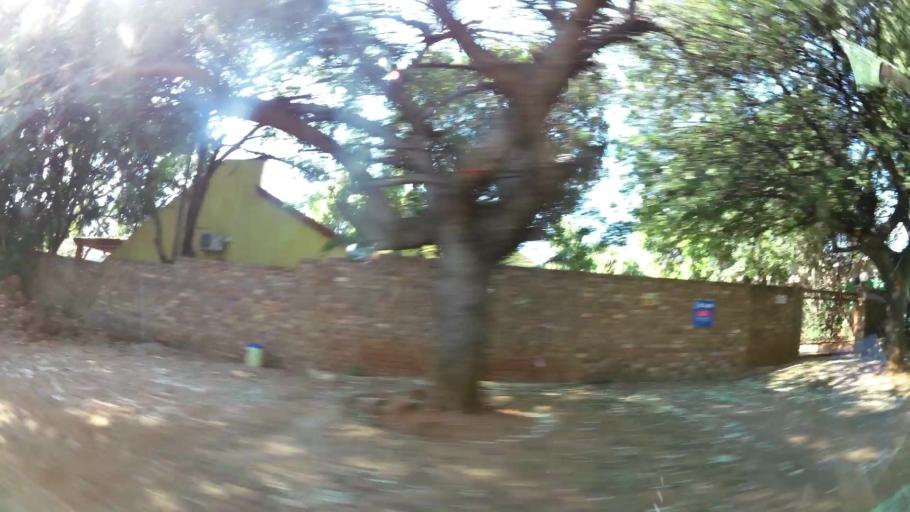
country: ZA
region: Gauteng
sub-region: City of Tshwane Metropolitan Municipality
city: Pretoria
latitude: -25.6849
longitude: 28.2333
